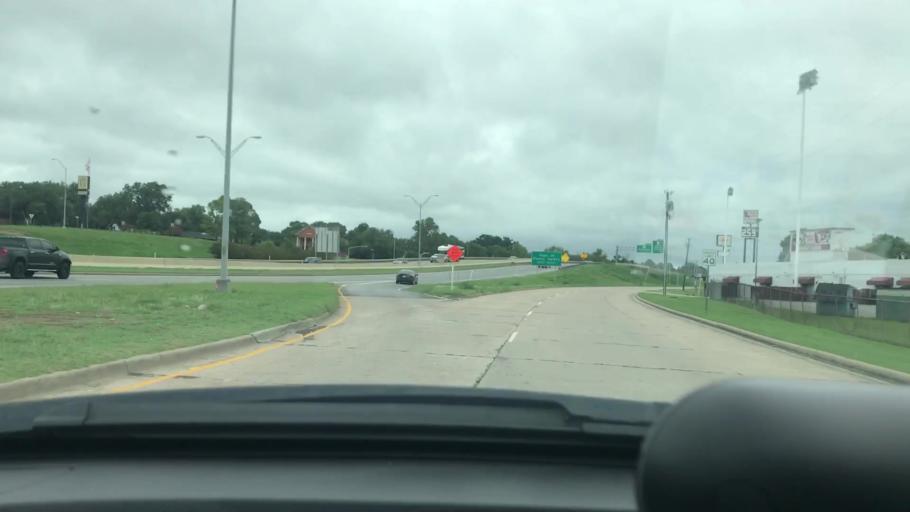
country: US
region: Texas
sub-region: Grayson County
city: Sherman
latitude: 33.6375
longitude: -96.6161
